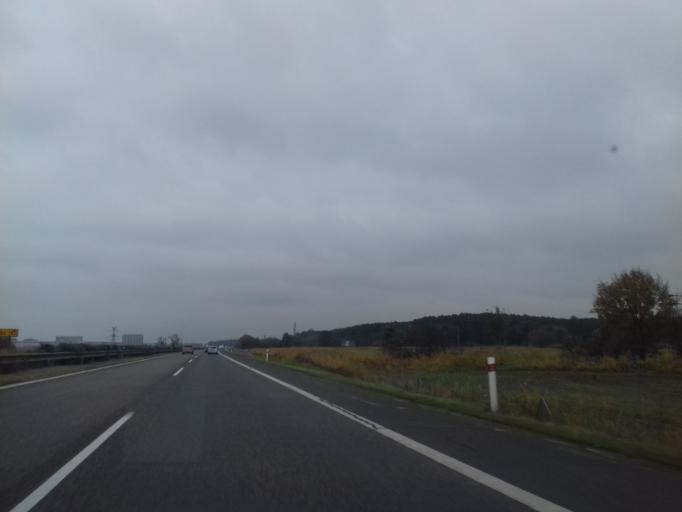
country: SK
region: Bratislavsky
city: Stupava
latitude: 48.3036
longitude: 17.0153
